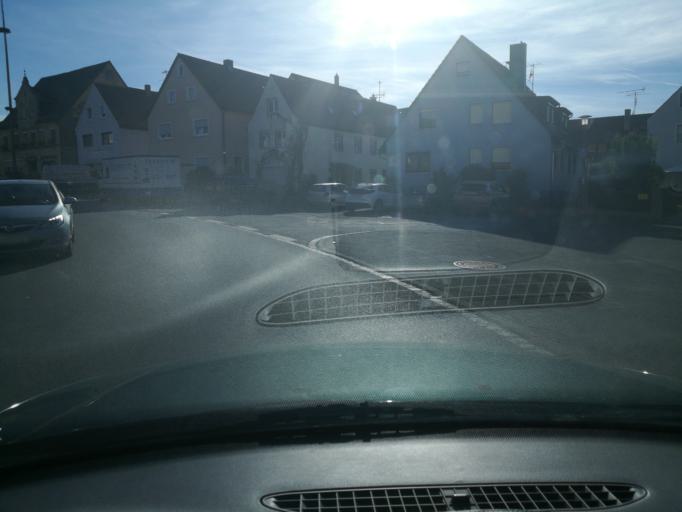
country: DE
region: Bavaria
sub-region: Regierungsbezirk Mittelfranken
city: Kalchreuth
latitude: 49.5587
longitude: 11.1327
